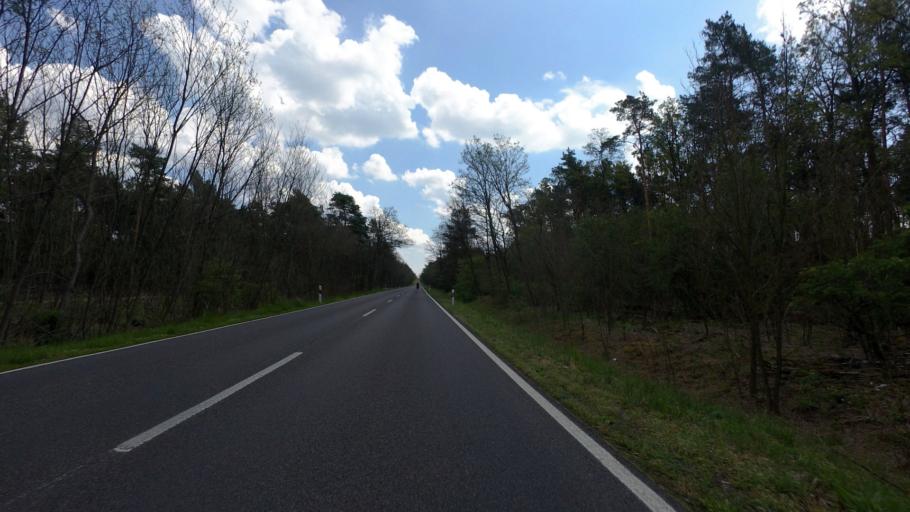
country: DE
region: Brandenburg
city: Neu Zauche
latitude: 51.9451
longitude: 14.0147
